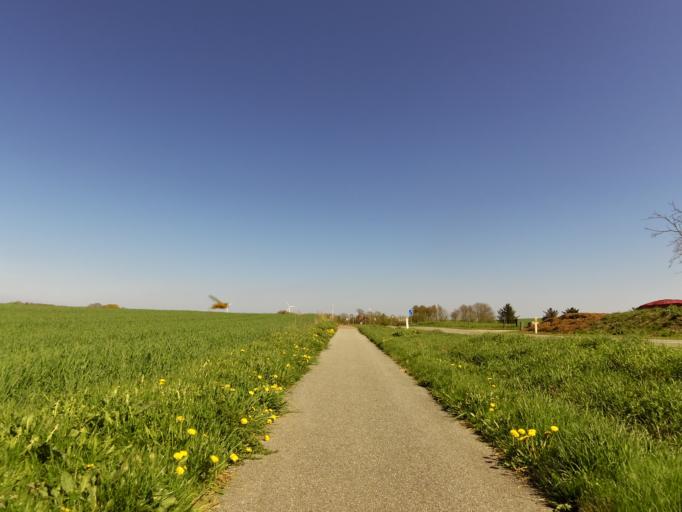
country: DK
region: Central Jutland
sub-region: Holstebro Kommune
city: Vinderup
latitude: 56.6002
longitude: 8.7525
